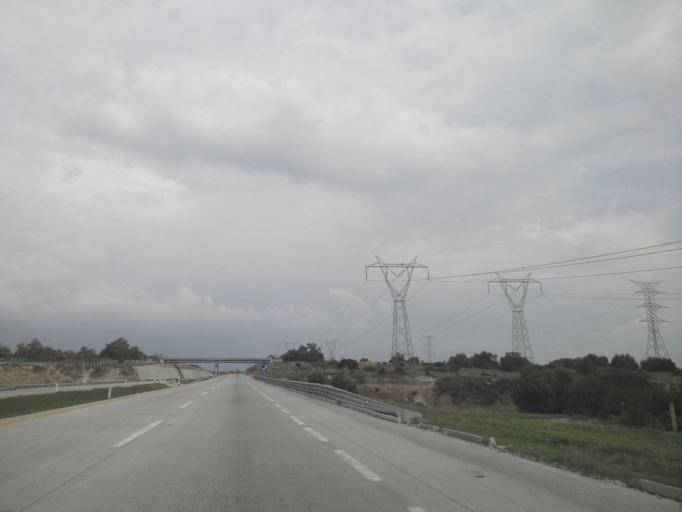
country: MX
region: Mexico
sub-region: Apaxco
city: Colonia Juarez
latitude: 20.0011
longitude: -99.1407
